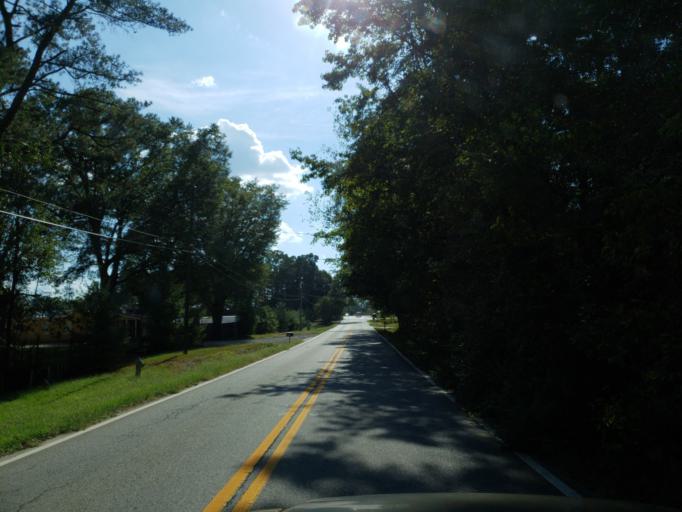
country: US
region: Georgia
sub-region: Cobb County
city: Mableton
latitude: 33.7795
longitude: -84.5442
